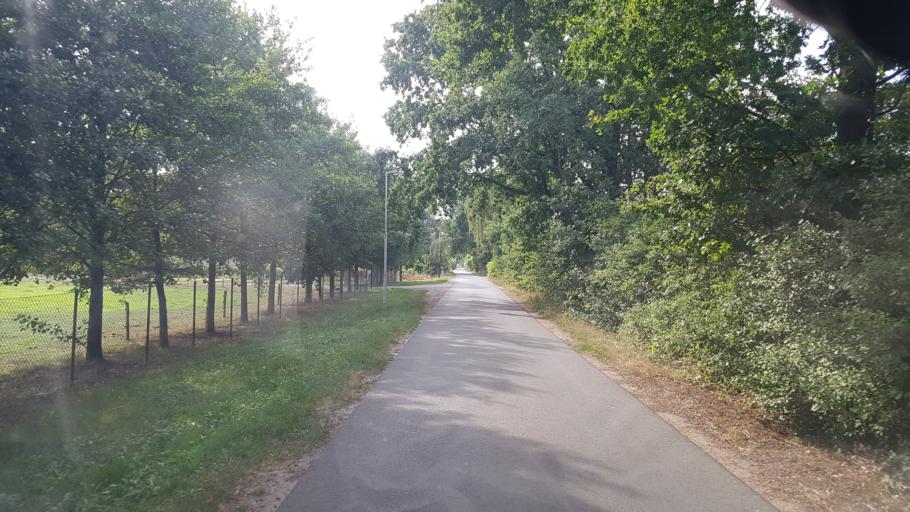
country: DE
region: Brandenburg
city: Plessa
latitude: 51.4417
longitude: 13.5939
